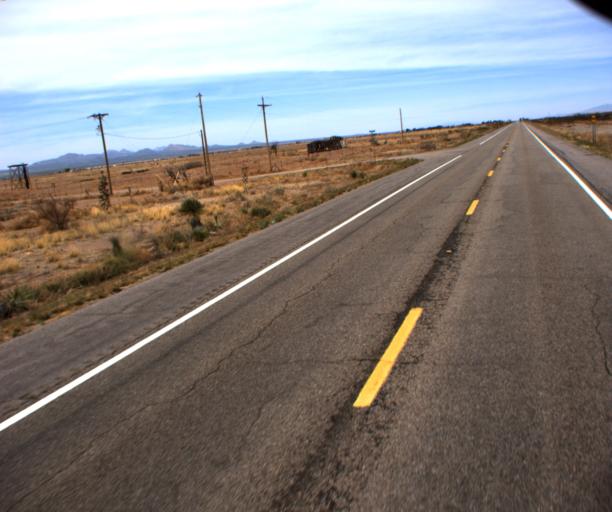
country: US
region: Arizona
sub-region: Cochise County
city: Pirtleville
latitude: 31.5686
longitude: -109.6679
